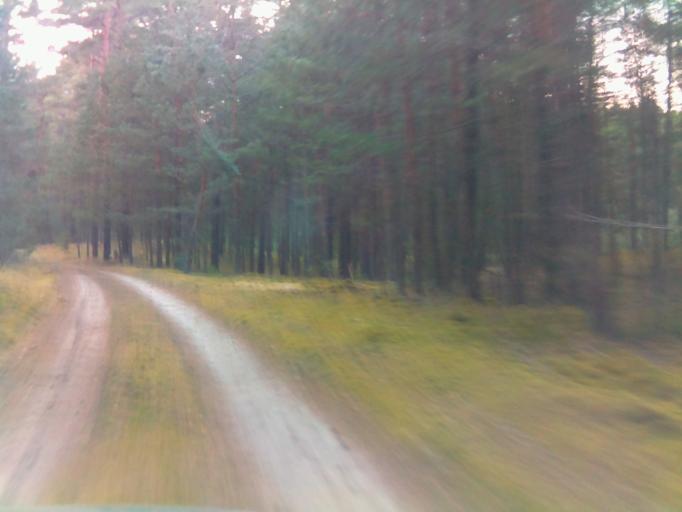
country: DE
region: Brandenburg
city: Jamlitz
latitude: 51.9764
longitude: 14.4148
